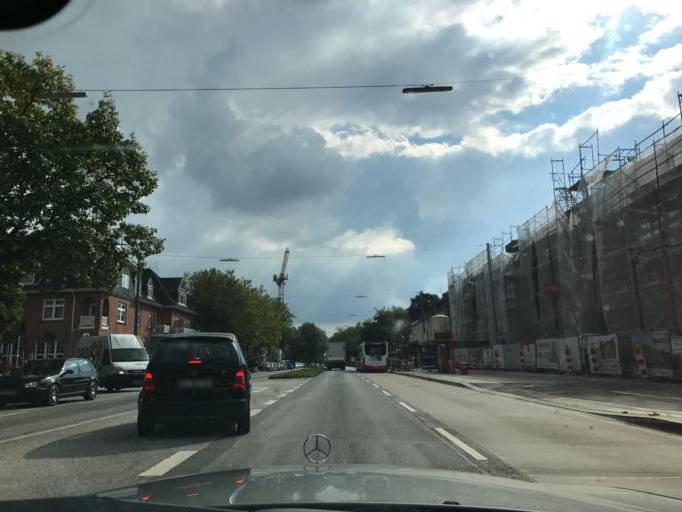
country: DE
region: Hamburg
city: Hamburg-Nord
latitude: 53.5941
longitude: 9.9666
